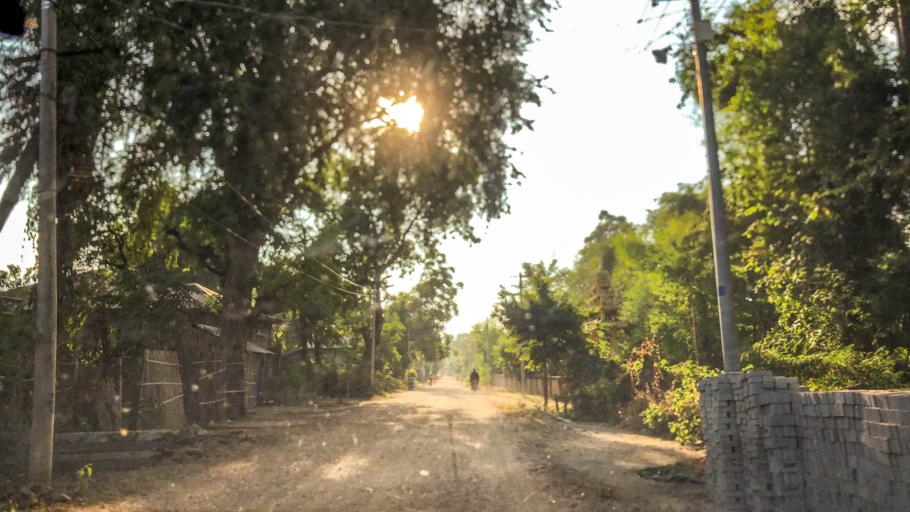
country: MM
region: Magway
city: Magway
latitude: 19.9748
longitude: 95.0367
